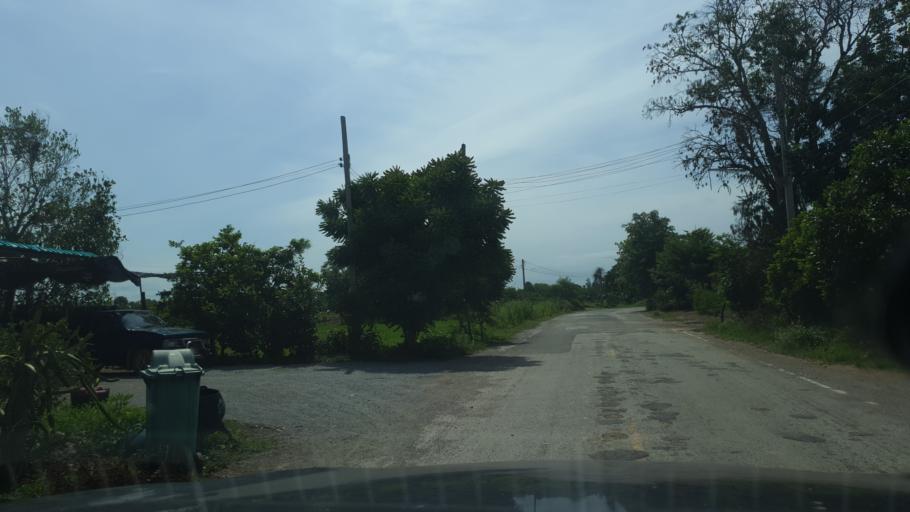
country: TH
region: Sukhothai
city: Si Samrong
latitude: 17.1965
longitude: 99.7291
